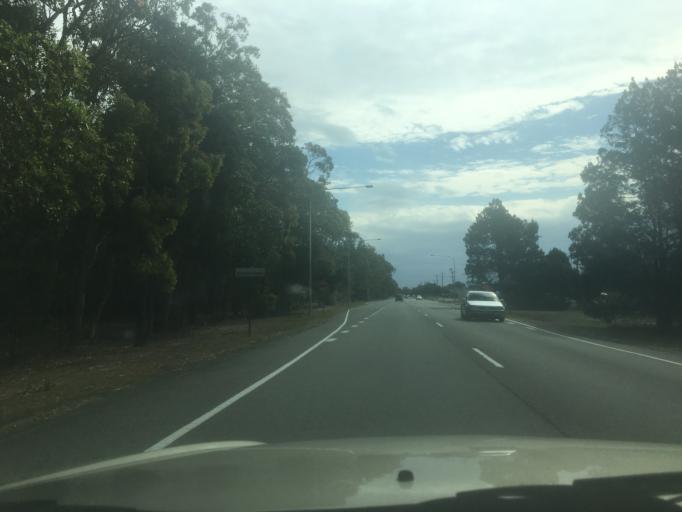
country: AU
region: Queensland
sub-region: Moreton Bay
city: Bongaree
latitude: -27.0778
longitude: 153.1820
